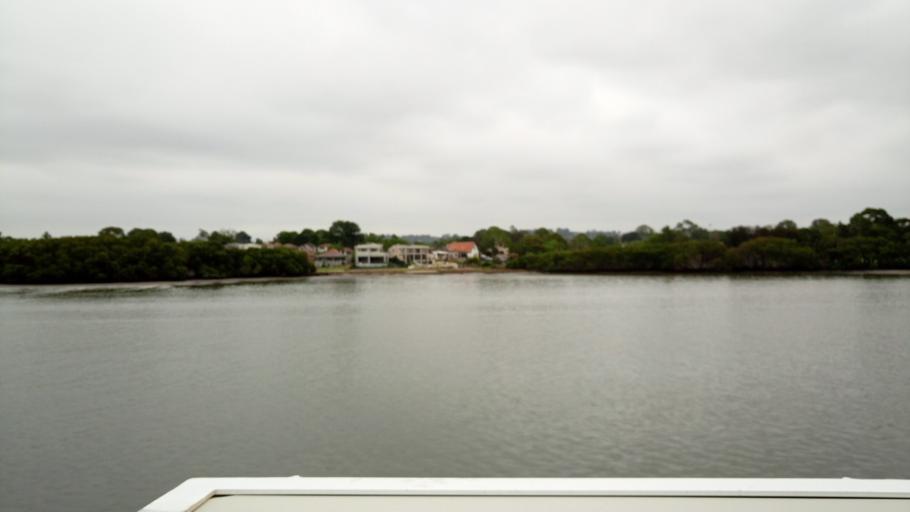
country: AU
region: New South Wales
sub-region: Canada Bay
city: Rhodes
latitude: -33.8217
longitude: 151.0811
